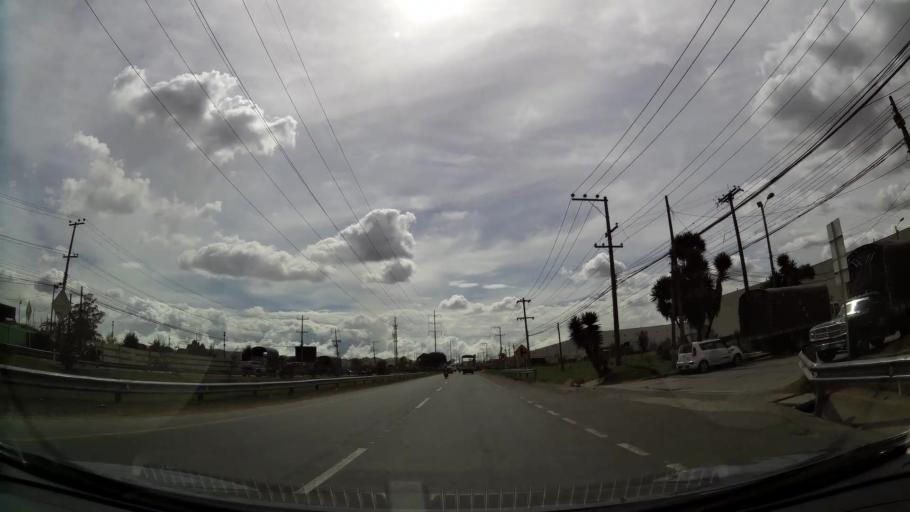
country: CO
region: Cundinamarca
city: Funza
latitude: 4.6986
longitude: -74.1941
